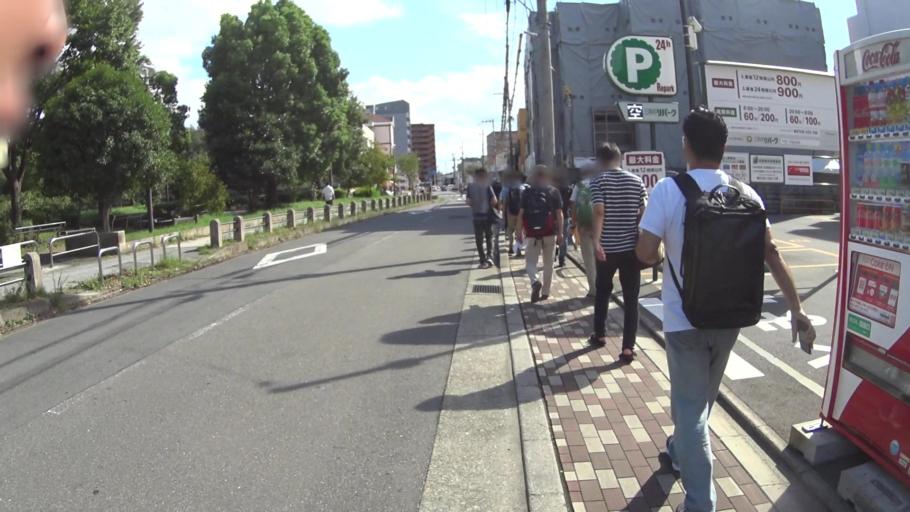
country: JP
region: Kyoto
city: Kyoto
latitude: 34.9983
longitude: 135.7426
